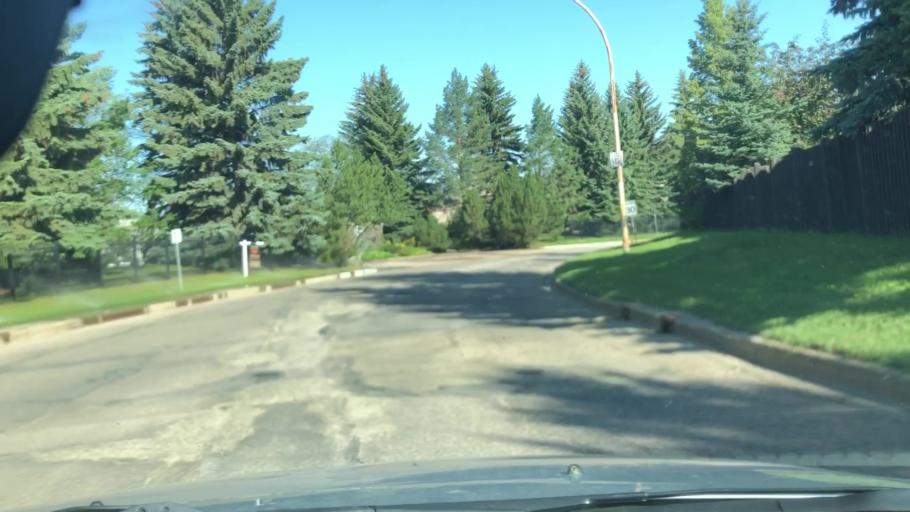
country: CA
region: Alberta
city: Edmonton
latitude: 53.4764
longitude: -113.6021
